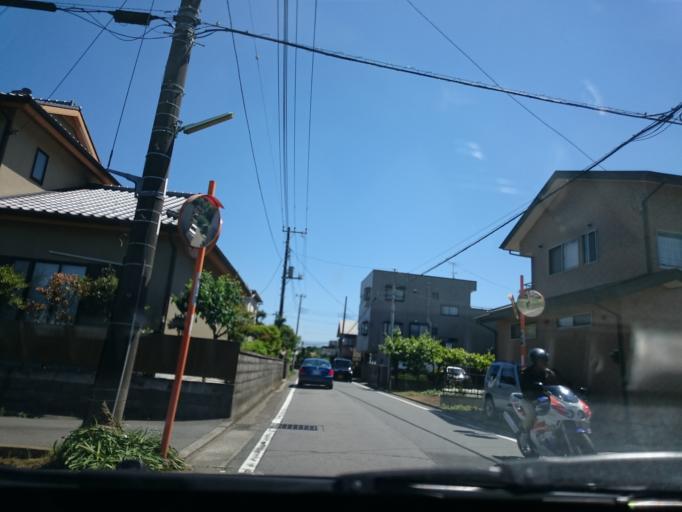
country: JP
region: Shizuoka
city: Mishima
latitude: 35.0531
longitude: 138.9325
